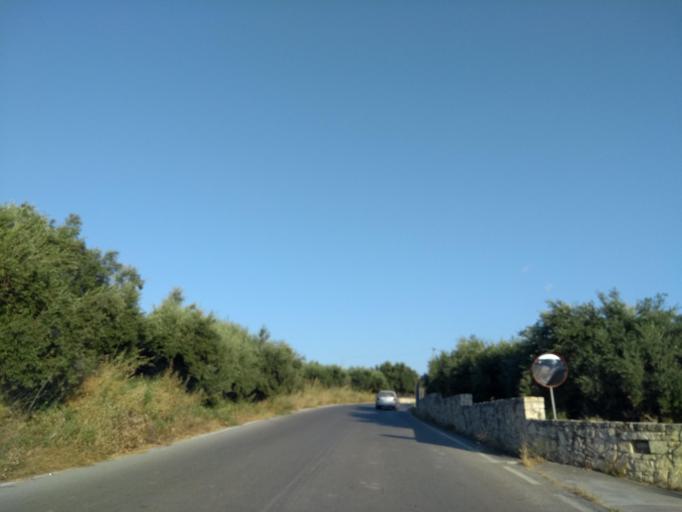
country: GR
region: Crete
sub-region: Nomos Chanias
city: Kalivai
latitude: 35.4447
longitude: 24.1755
